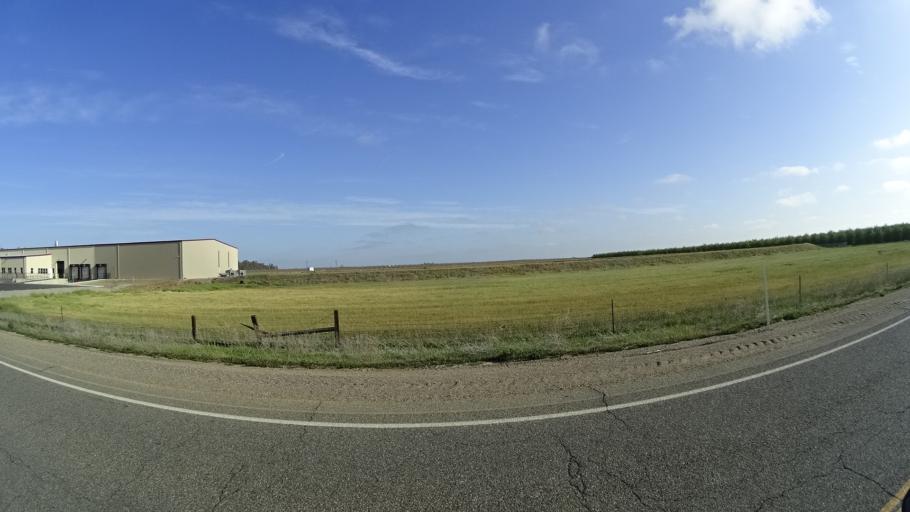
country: US
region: California
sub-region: Glenn County
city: Willows
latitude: 39.5838
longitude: -122.1892
